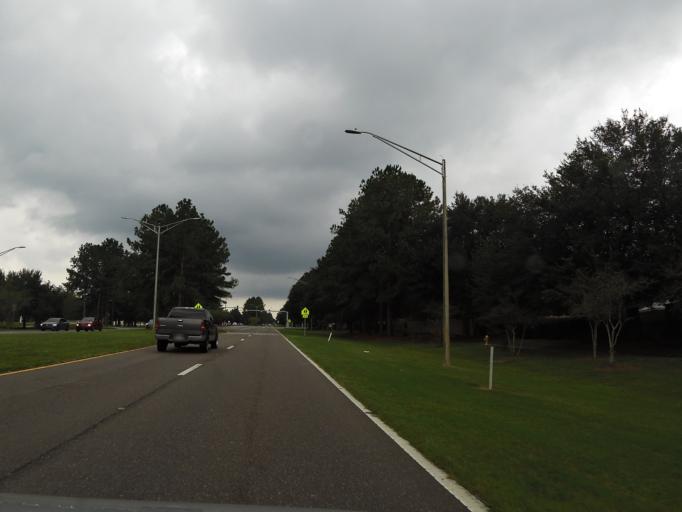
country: US
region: Florida
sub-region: Clay County
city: Bellair-Meadowbrook Terrace
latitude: 30.1984
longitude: -81.8070
